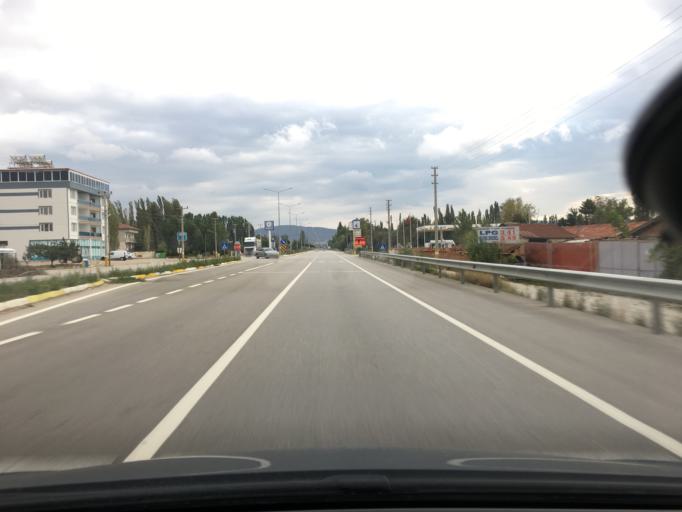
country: TR
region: Afyonkarahisar
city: Sincanli
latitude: 38.7706
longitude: 30.3687
